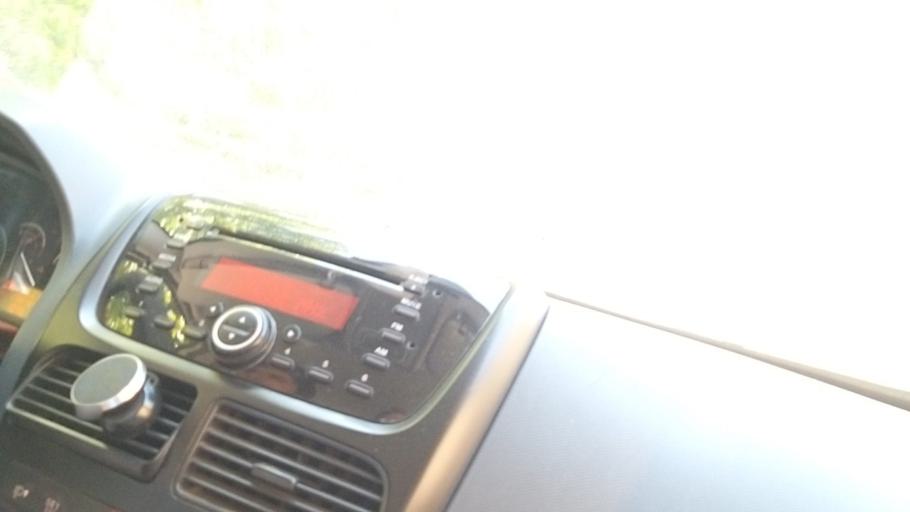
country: TR
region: Batman
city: Kozluk
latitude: 38.2181
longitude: 41.4848
